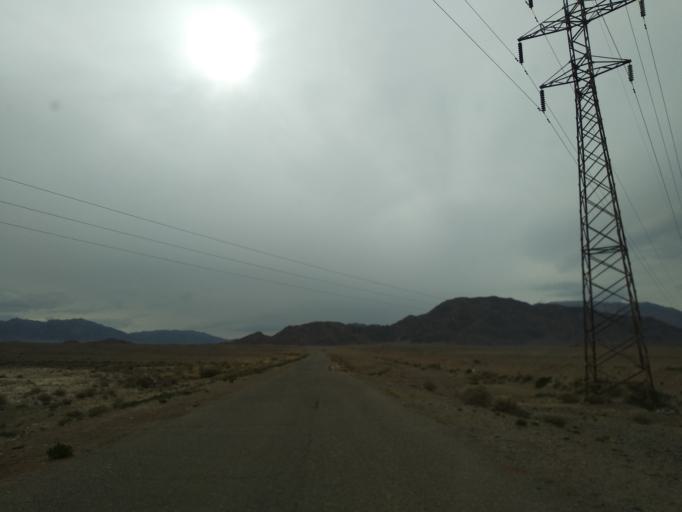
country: KG
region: Ysyk-Koel
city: Balykchy
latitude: 42.3202
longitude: 76.1826
